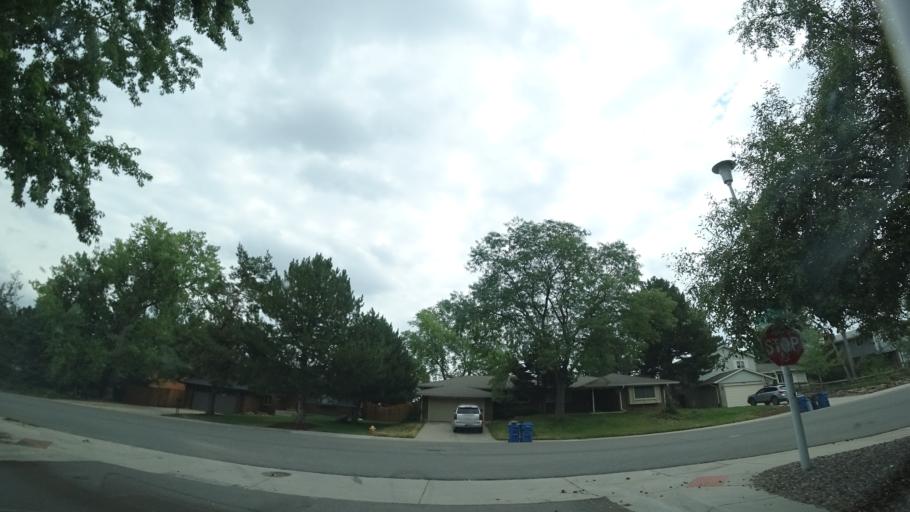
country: US
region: Colorado
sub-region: Jefferson County
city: West Pleasant View
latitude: 39.7233
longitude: -105.1555
